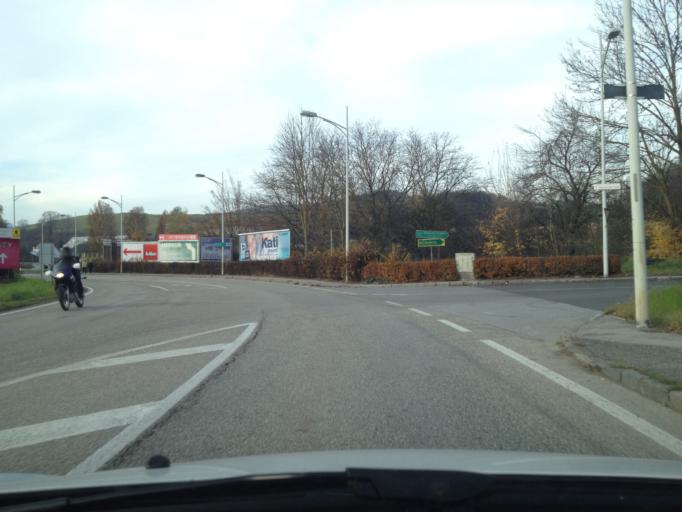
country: AT
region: Upper Austria
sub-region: Politischer Bezirk Urfahr-Umgebung
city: Altenberg bei Linz
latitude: 48.3273
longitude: 14.3360
